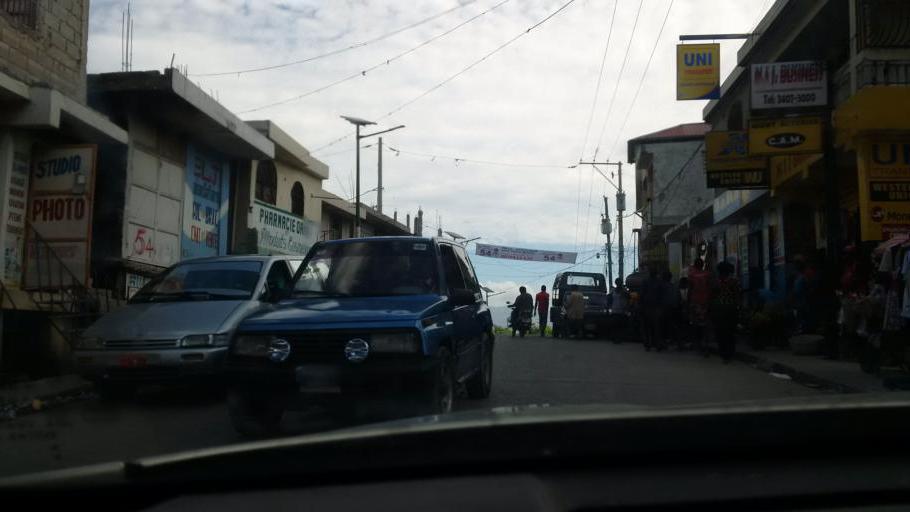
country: HT
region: Ouest
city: Delmas 73
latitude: 18.5456
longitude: -72.3071
